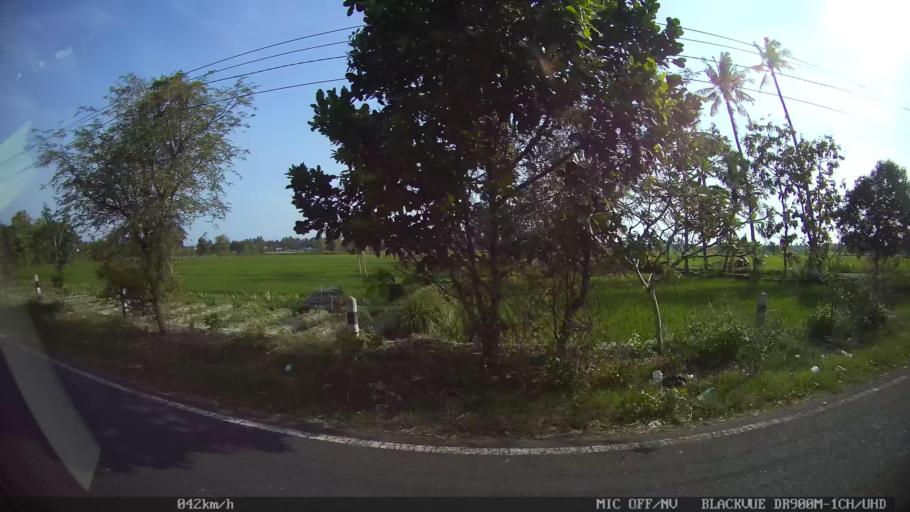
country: ID
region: Daerah Istimewa Yogyakarta
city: Pandak
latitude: -7.9030
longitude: 110.3062
